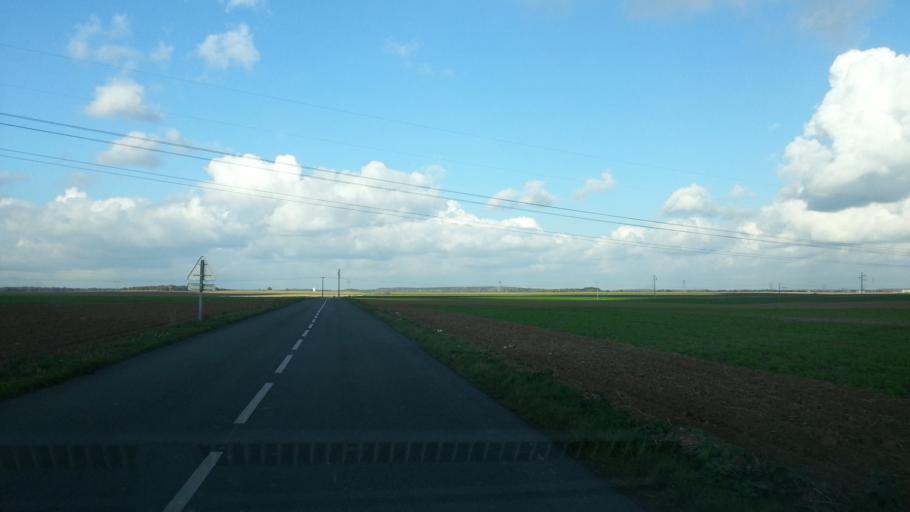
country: FR
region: Picardie
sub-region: Departement de l'Oise
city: Villers-sous-Saint-Leu
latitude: 49.2298
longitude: 2.4131
